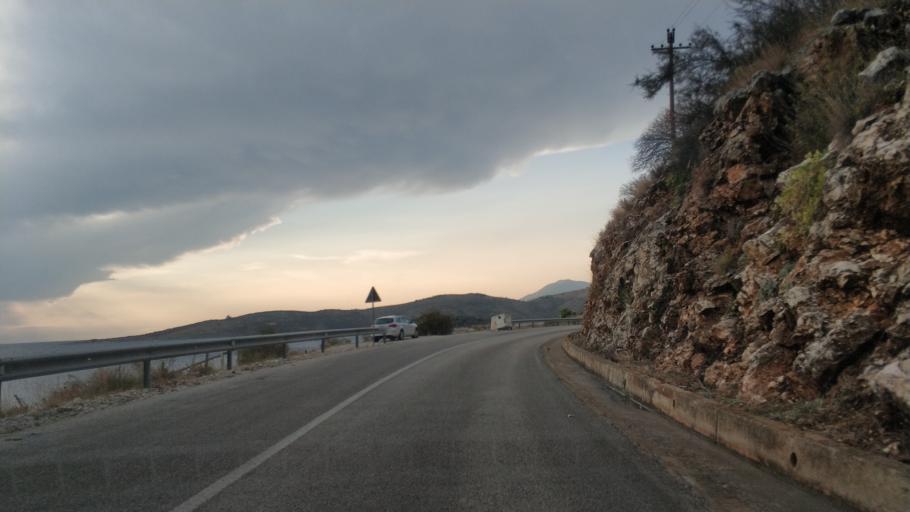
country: AL
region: Vlore
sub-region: Rrethi i Vlores
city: Himare
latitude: 40.0572
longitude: 19.8030
